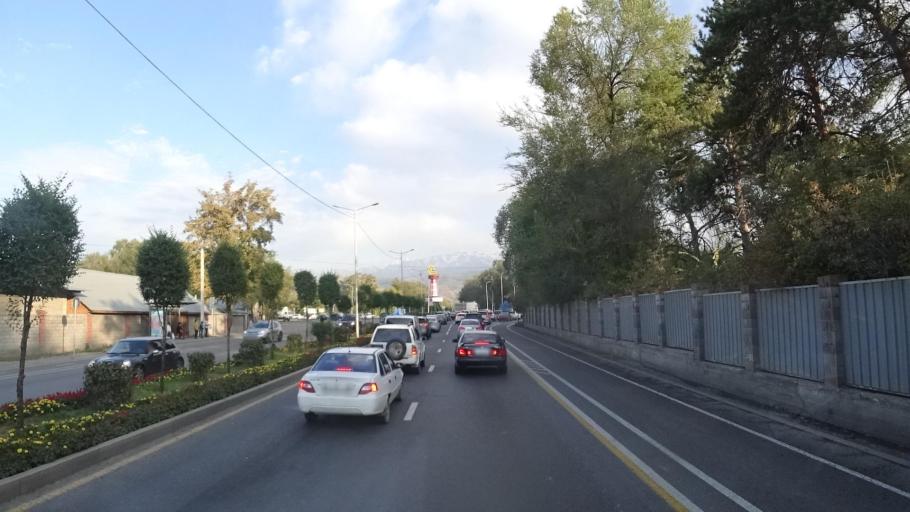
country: KZ
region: Almaty Oblysy
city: Pervomayskiy
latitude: 43.3207
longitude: 77.0242
